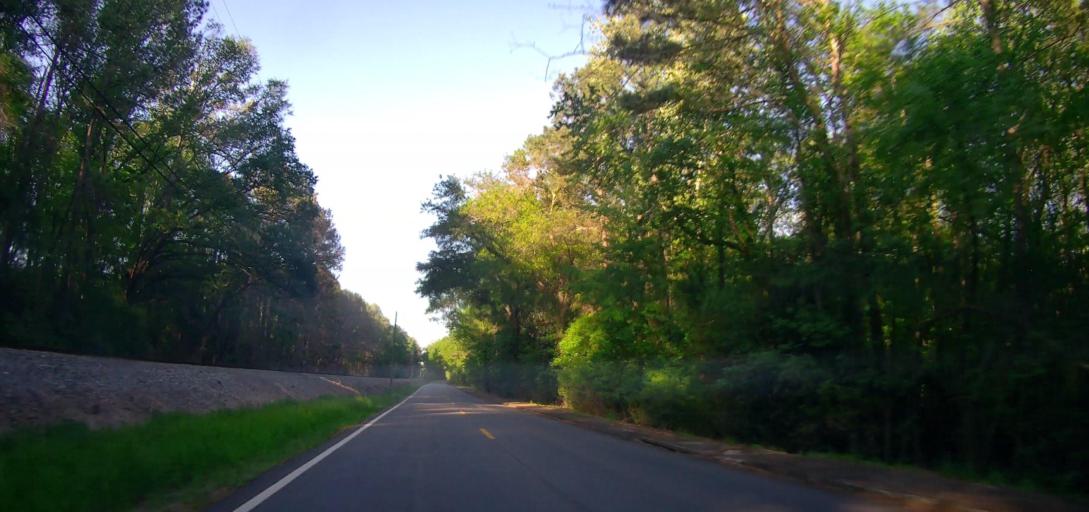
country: US
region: Georgia
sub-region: Macon County
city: Montezuma
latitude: 32.3059
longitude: -84.0213
